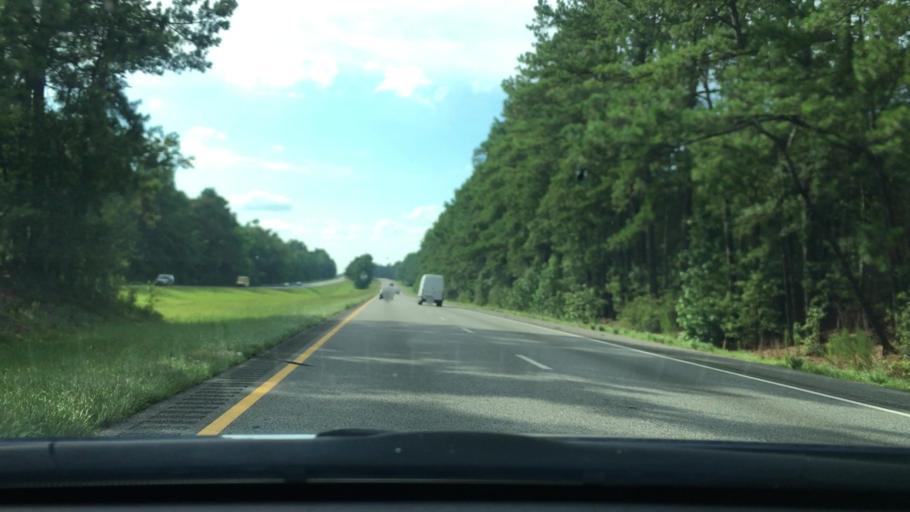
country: US
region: South Carolina
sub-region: Dorchester County
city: Ridgeville
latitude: 33.1643
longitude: -80.3579
